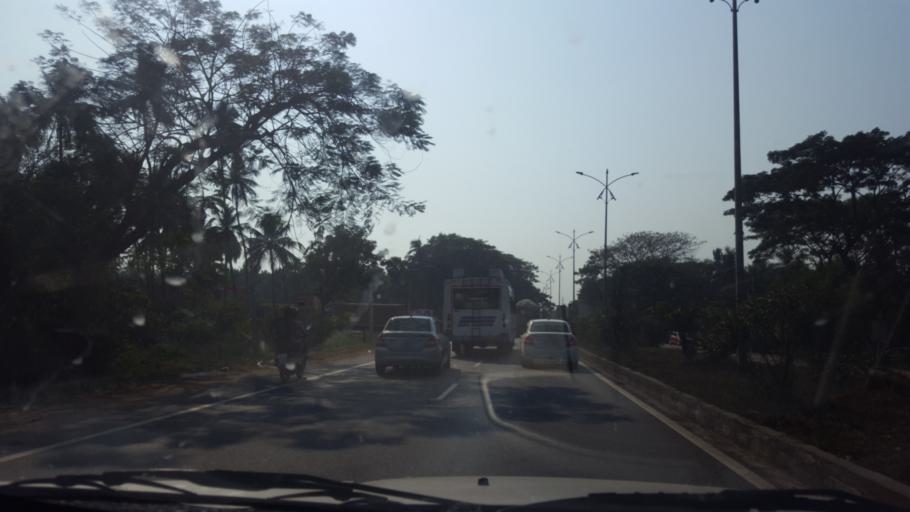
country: IN
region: Andhra Pradesh
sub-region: Vishakhapatnam
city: Anakapalle
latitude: 17.6757
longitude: 83.0120
